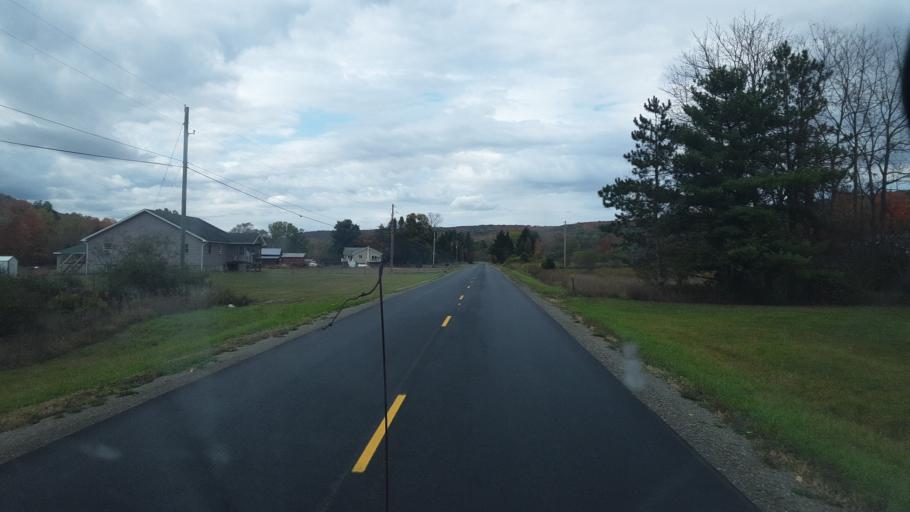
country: US
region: New York
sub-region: Allegany County
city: Alfred
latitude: 42.3679
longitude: -77.7858
